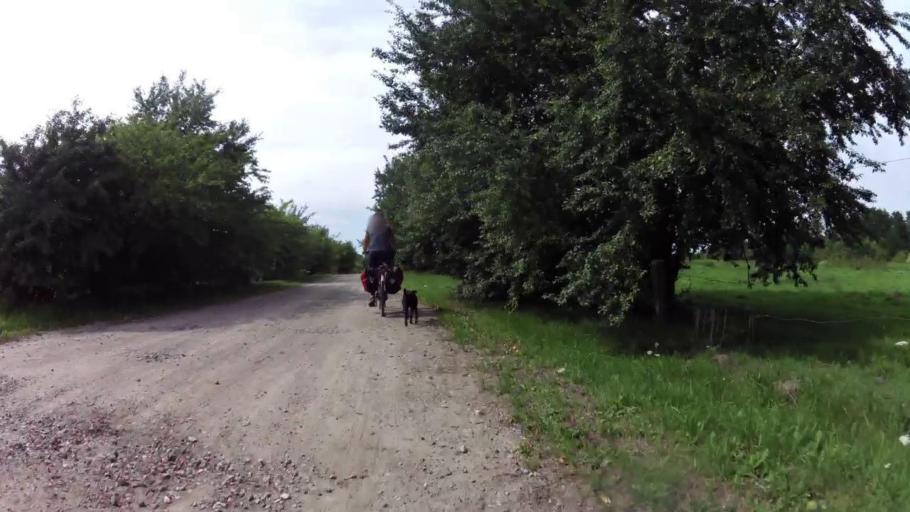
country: PL
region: West Pomeranian Voivodeship
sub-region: Powiat lobeski
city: Wegorzyno
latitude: 53.5374
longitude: 15.6081
